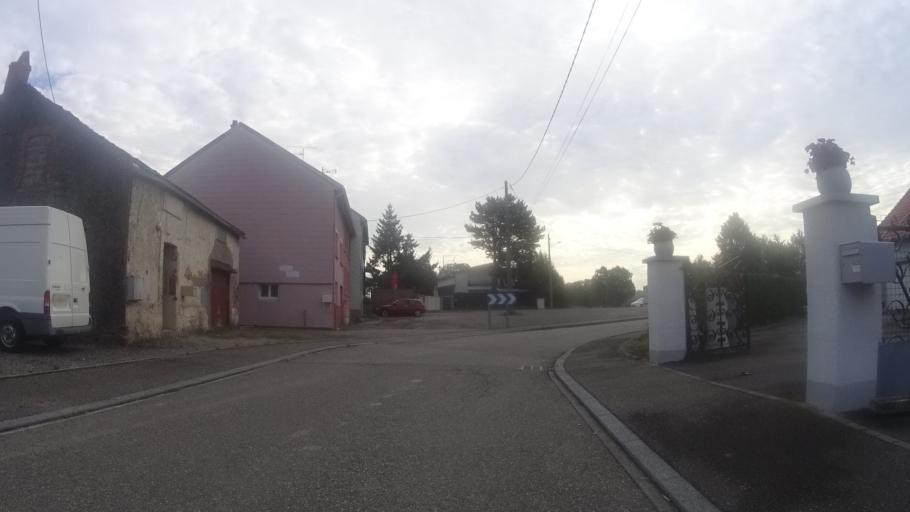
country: FR
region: Lorraine
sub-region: Departement de la Moselle
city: Niderviller
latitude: 48.7103
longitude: 7.0971
